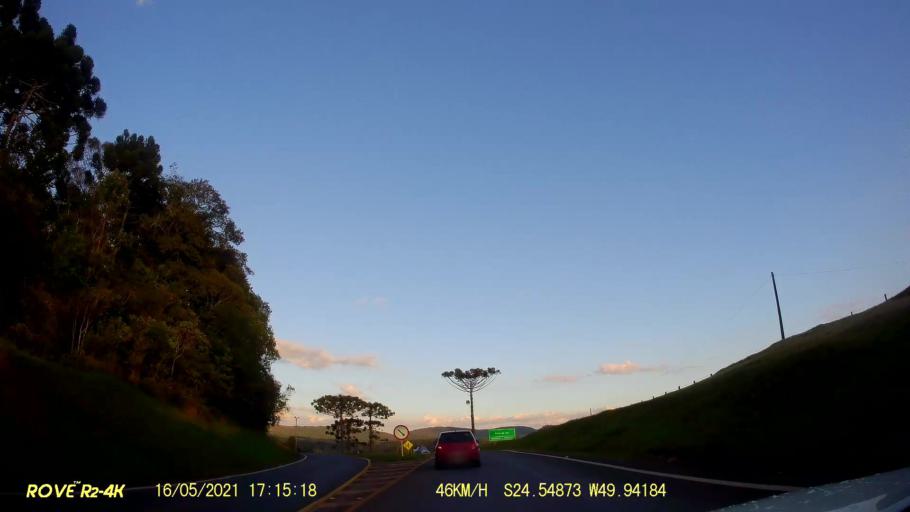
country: BR
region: Parana
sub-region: Pirai Do Sul
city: Pirai do Sul
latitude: -24.5488
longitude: -49.9418
